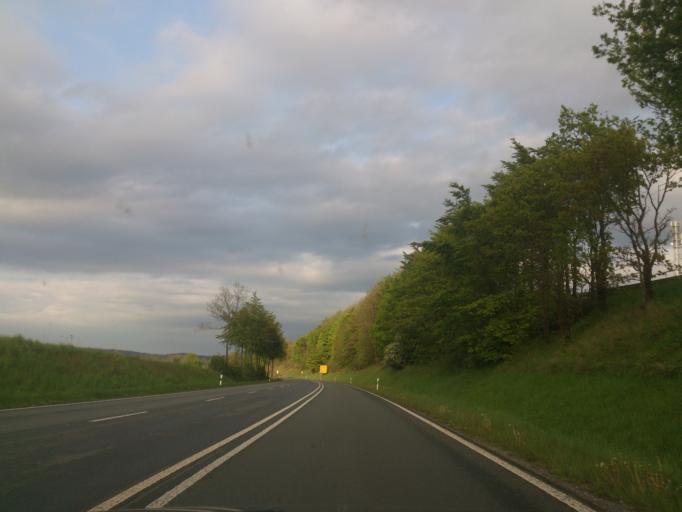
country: DE
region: North Rhine-Westphalia
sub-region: Regierungsbezirk Detmold
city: Altenbeken
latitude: 51.7249
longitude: 8.9016
